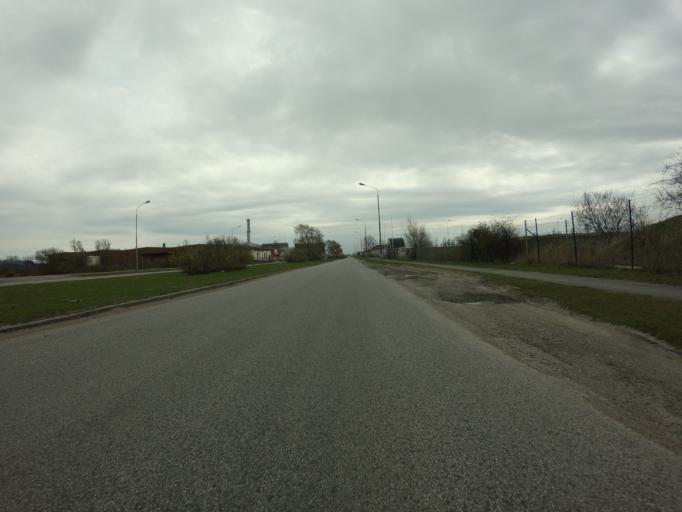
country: SE
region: Skane
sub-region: Burlovs Kommun
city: Arloev
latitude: 55.6318
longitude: 13.0356
